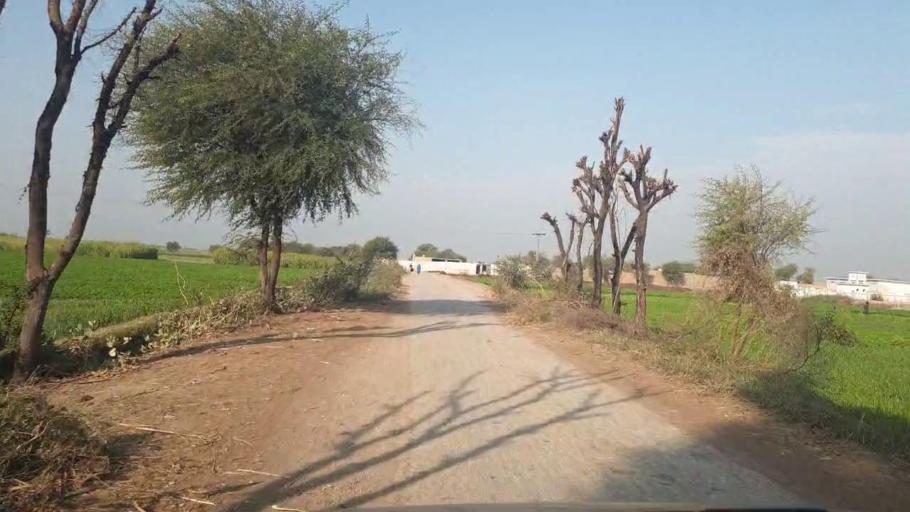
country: PK
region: Sindh
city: Tando Adam
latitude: 25.7367
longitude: 68.6155
